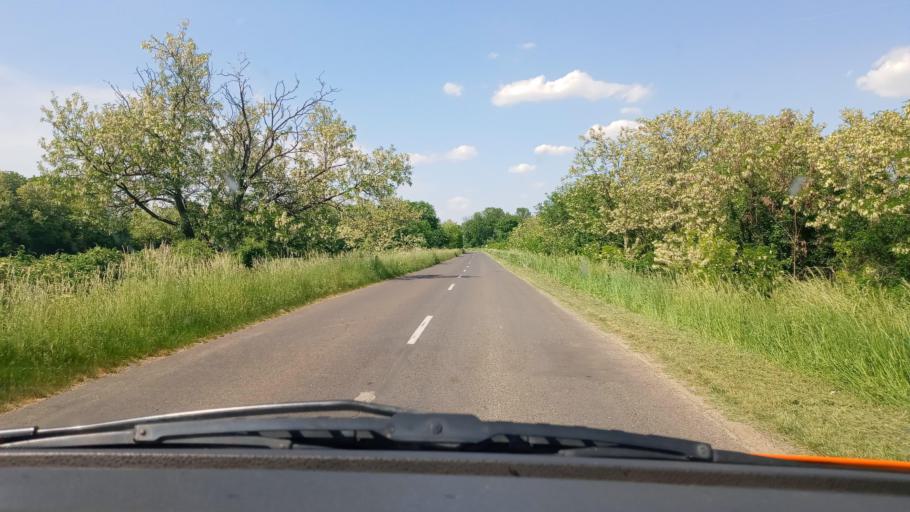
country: HU
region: Baranya
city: Harkany
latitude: 45.8906
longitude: 18.1716
